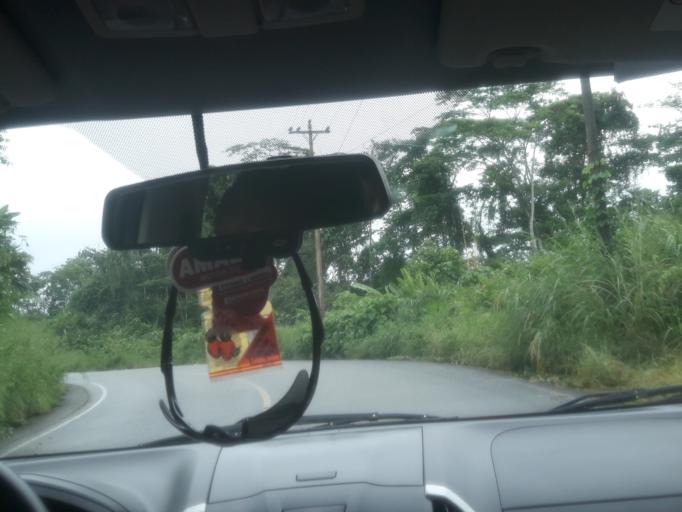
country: EC
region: Napo
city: Tena
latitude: -1.0338
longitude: -77.7298
